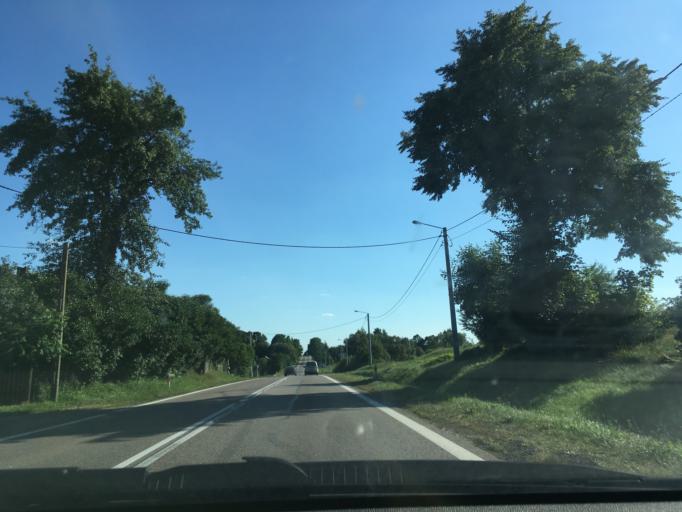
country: PL
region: Podlasie
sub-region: Powiat sokolski
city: Suchowola
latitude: 53.4922
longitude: 23.0954
